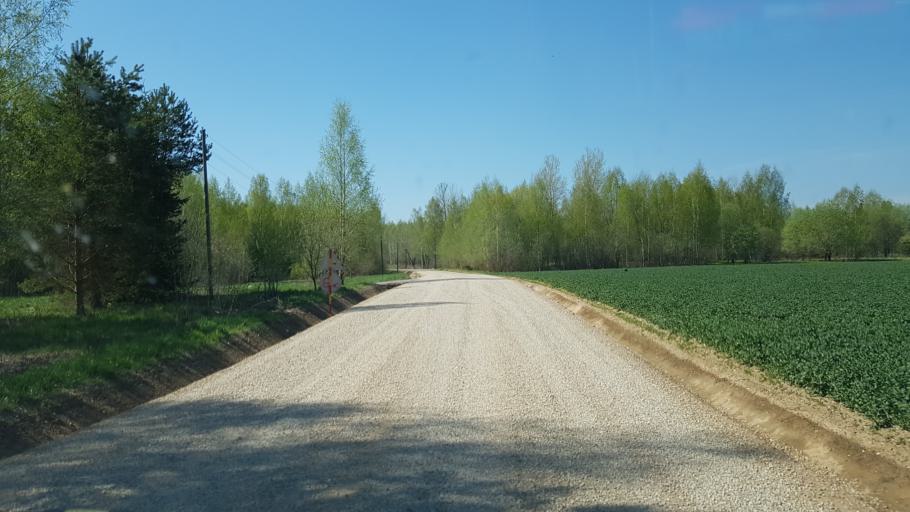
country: EE
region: Polvamaa
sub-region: Polva linn
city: Polva
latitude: 58.1225
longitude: 27.2430
